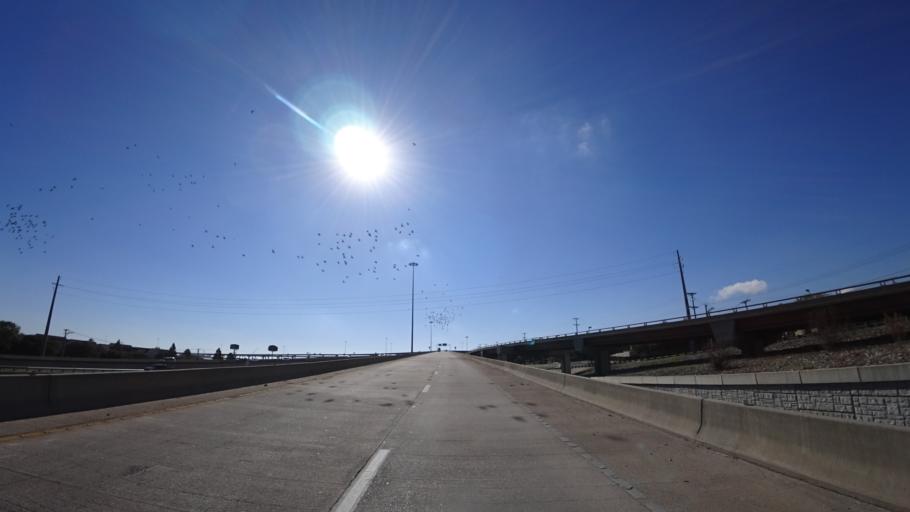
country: US
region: Texas
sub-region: Williamson County
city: Round Rock
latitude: 30.4874
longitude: -97.6766
